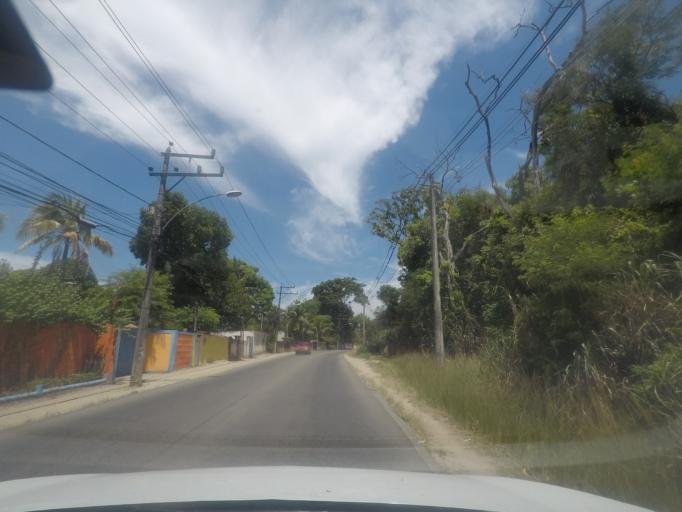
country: BR
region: Rio de Janeiro
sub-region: Itaguai
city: Itaguai
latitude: -22.9851
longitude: -43.6567
